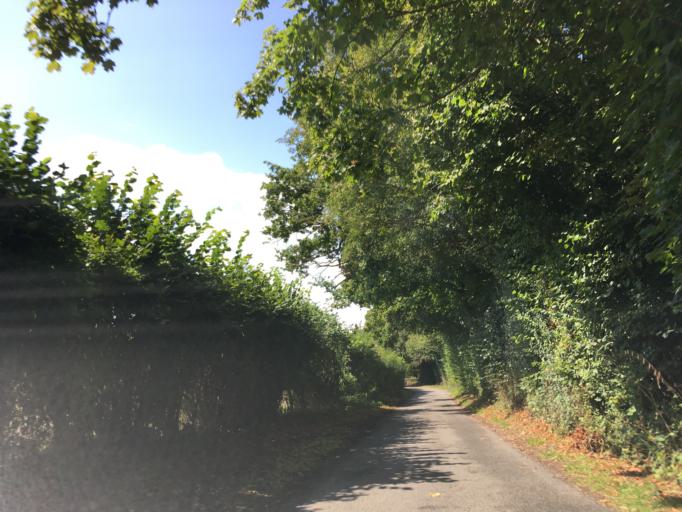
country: GB
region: England
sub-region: Hampshire
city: Colden Common
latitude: 51.0135
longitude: -1.2760
